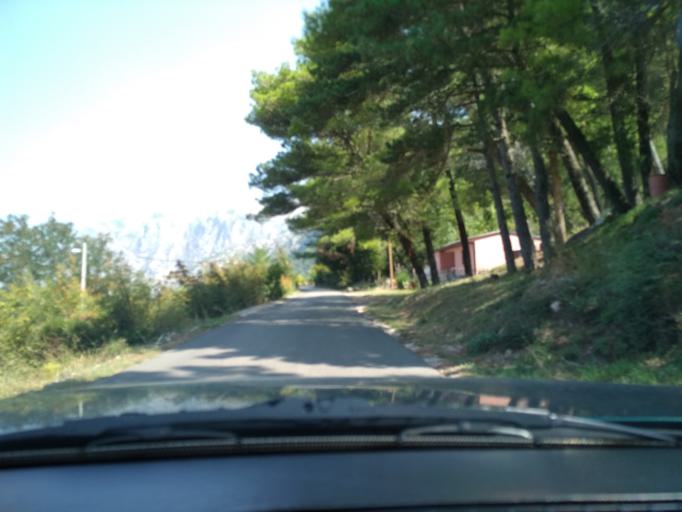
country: ME
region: Kotor
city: Kotor
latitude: 42.3982
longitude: 18.7681
